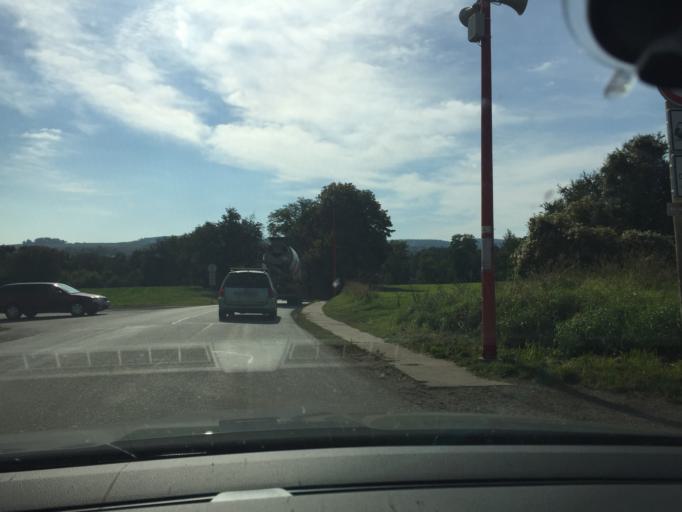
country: CZ
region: Central Bohemia
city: Cervene Pecky
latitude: 49.9881
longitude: 15.2077
